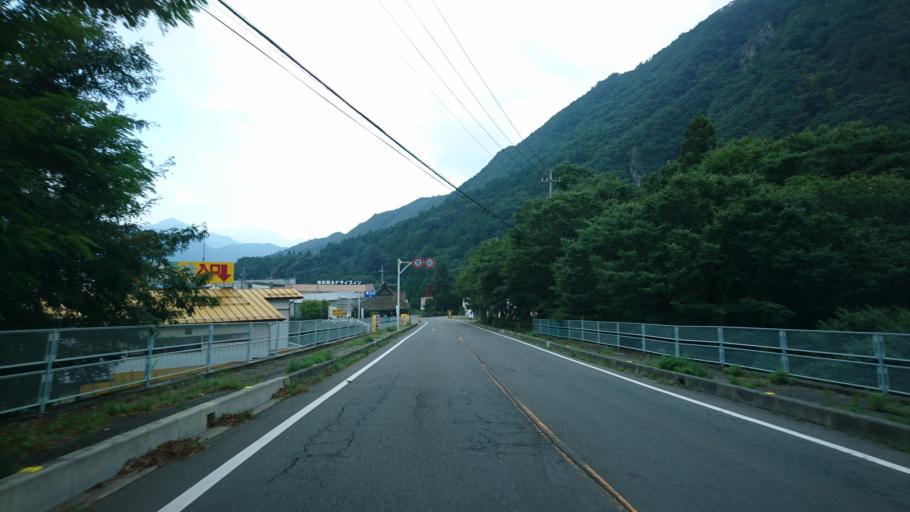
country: JP
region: Gunma
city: Numata
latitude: 36.7029
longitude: 139.2088
